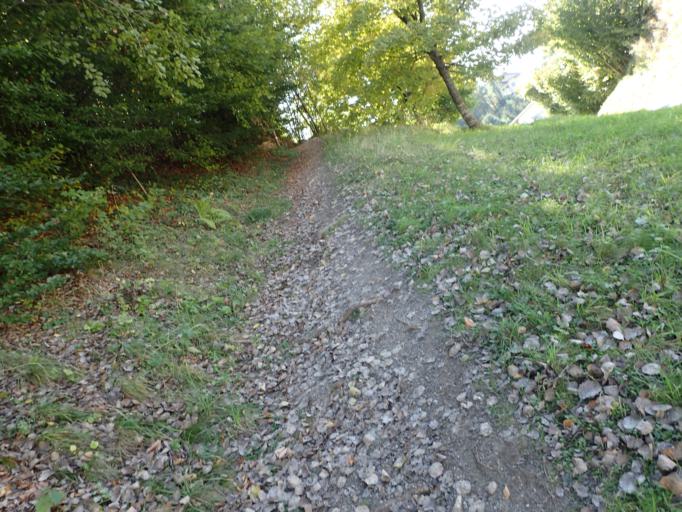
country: AT
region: Carinthia
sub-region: Politischer Bezirk Klagenfurt Land
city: Maria Worth
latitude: 46.6385
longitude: 14.1363
